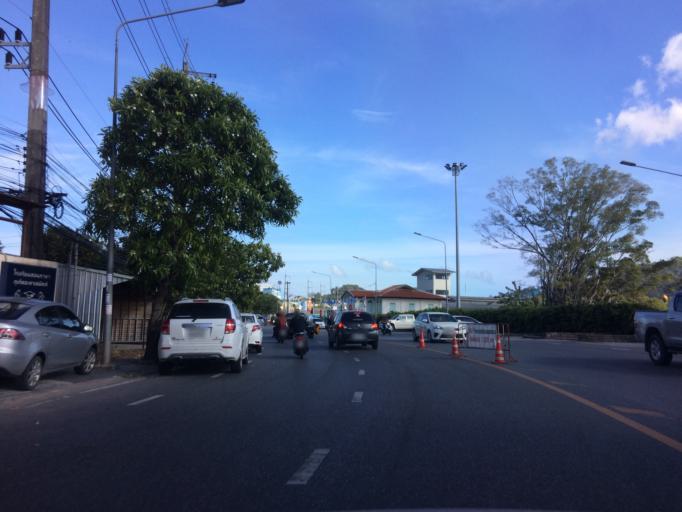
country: TH
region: Phuket
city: Kathu
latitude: 7.9049
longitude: 98.3513
